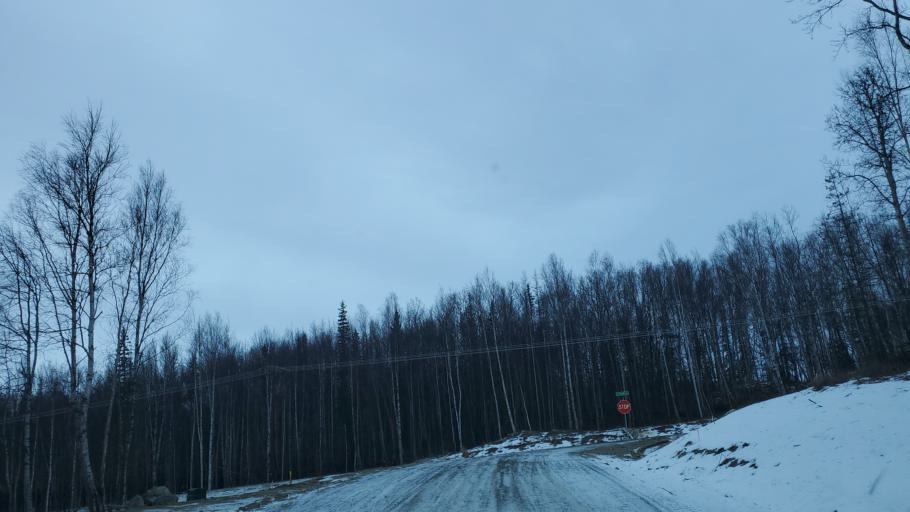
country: US
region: Alaska
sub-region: Matanuska-Susitna Borough
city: Gateway
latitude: 61.6567
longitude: -149.2363
